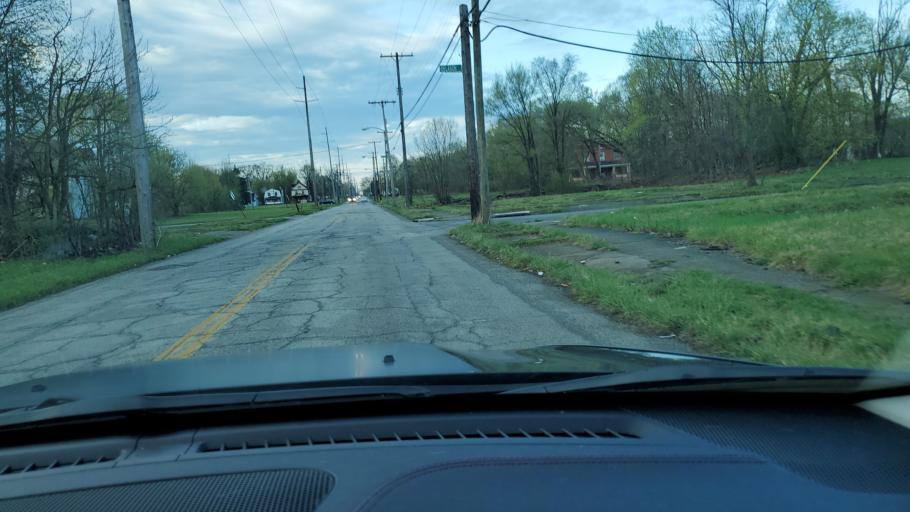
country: US
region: Ohio
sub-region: Mahoning County
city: Youngstown
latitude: 41.0832
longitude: -80.6640
